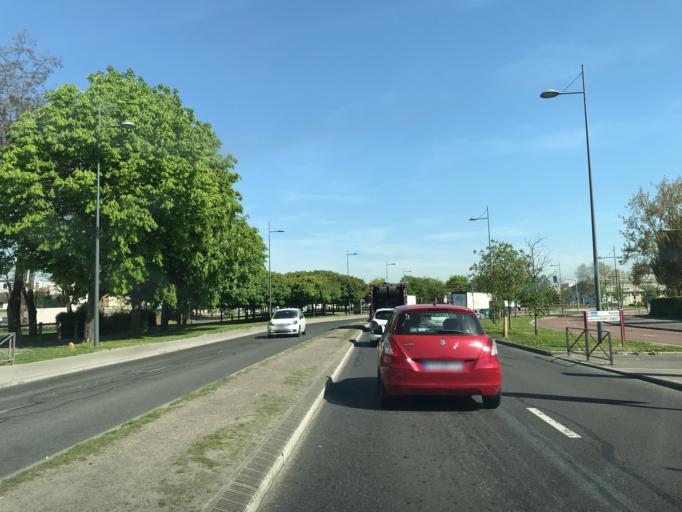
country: FR
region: Ile-de-France
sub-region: Departement du Val-de-Marne
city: Bonneuil-sur-Marne
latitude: 48.7720
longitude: 2.4902
